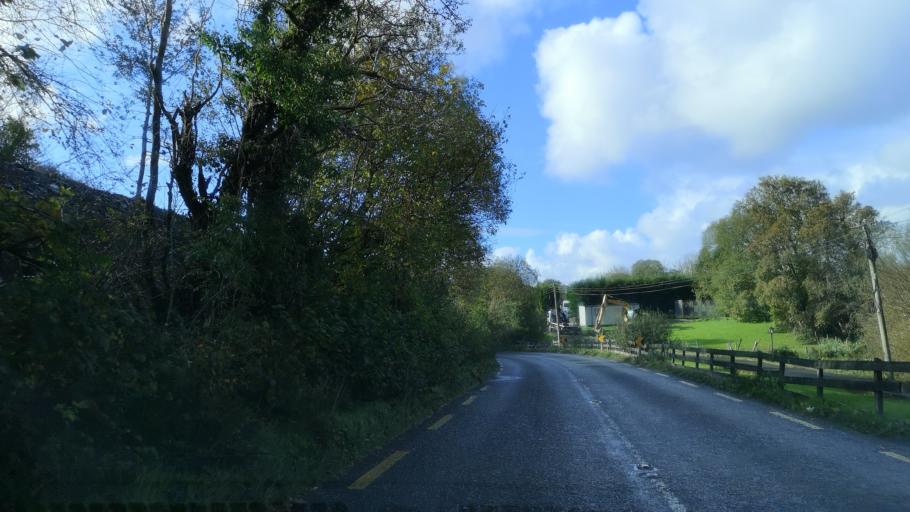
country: IE
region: Connaught
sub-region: Maigh Eo
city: Westport
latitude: 53.7869
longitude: -9.4678
